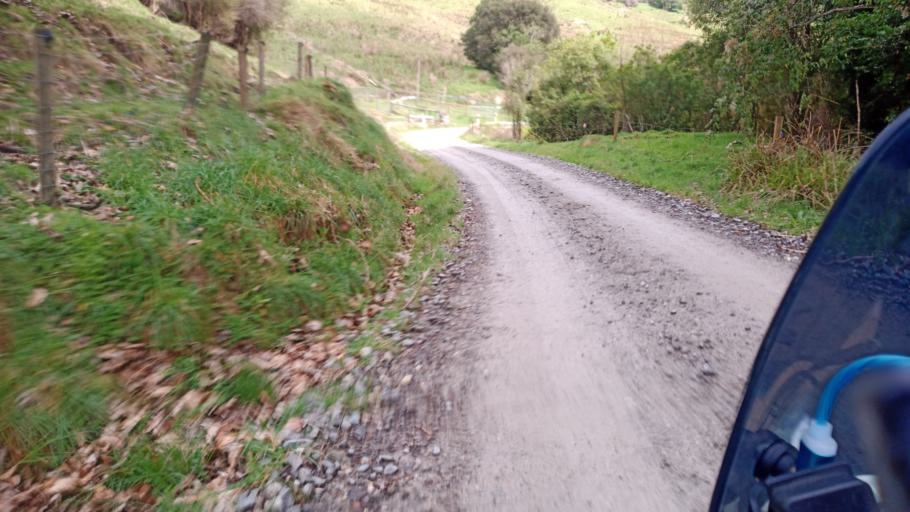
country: NZ
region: Gisborne
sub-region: Gisborne District
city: Gisborne
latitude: -38.5471
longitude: 178.1332
